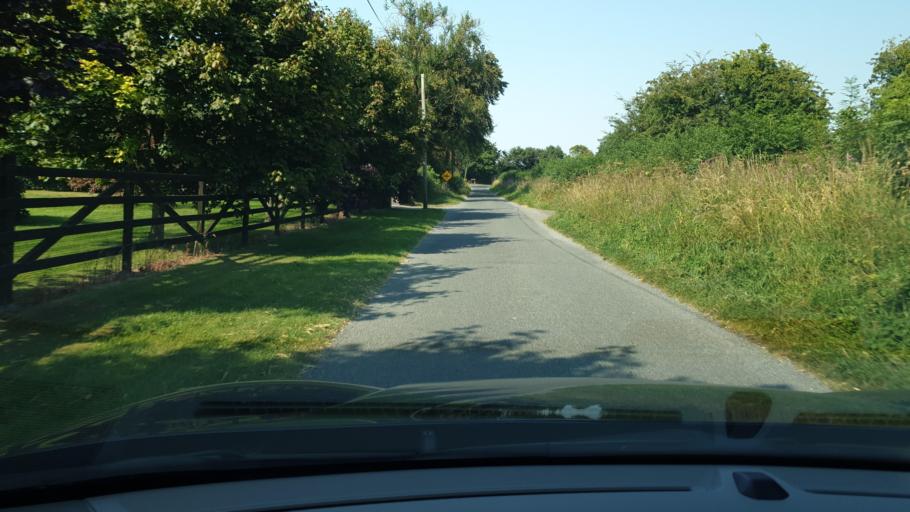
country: IE
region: Leinster
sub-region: An Mhi
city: Athboy
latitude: 53.6343
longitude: -6.9809
